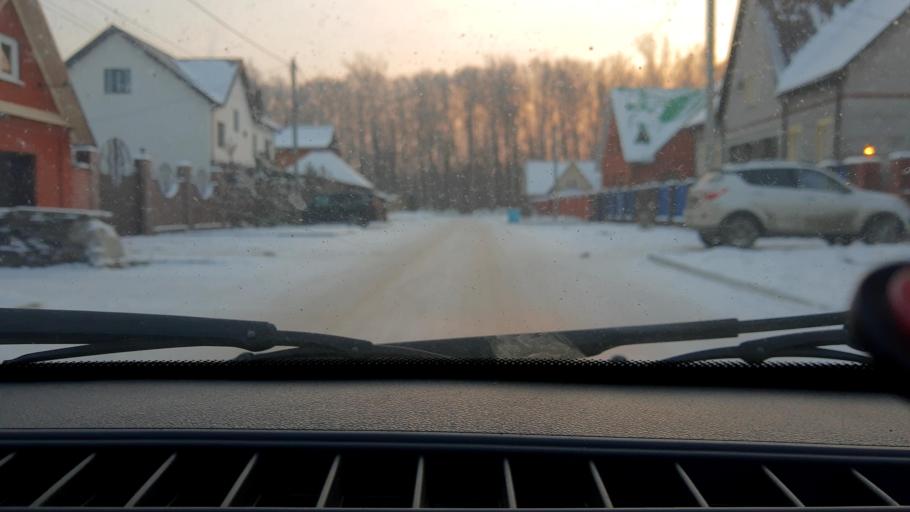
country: RU
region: Bashkortostan
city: Ufa
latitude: 54.7893
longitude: 56.1614
